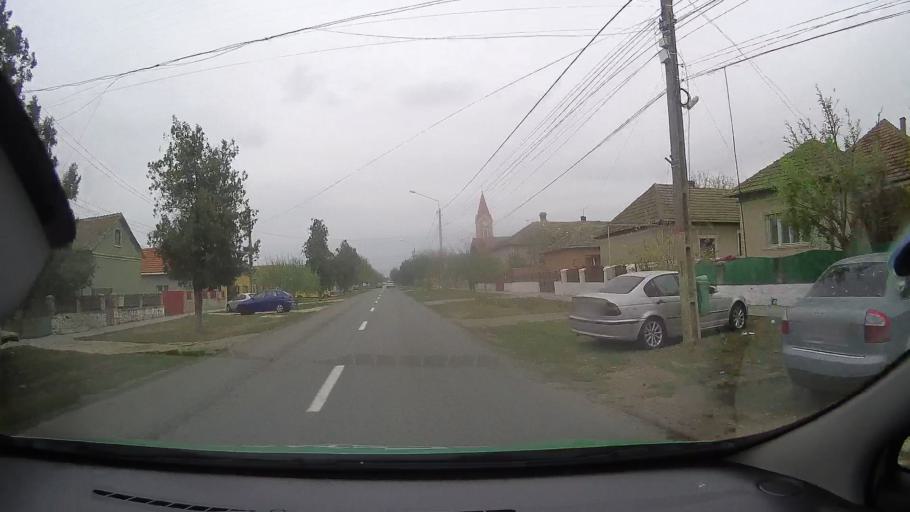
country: RO
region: Constanta
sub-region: Comuna Mihail Kogalniceanu
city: Mihail Kogalniceanu
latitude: 44.3720
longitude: 28.4638
